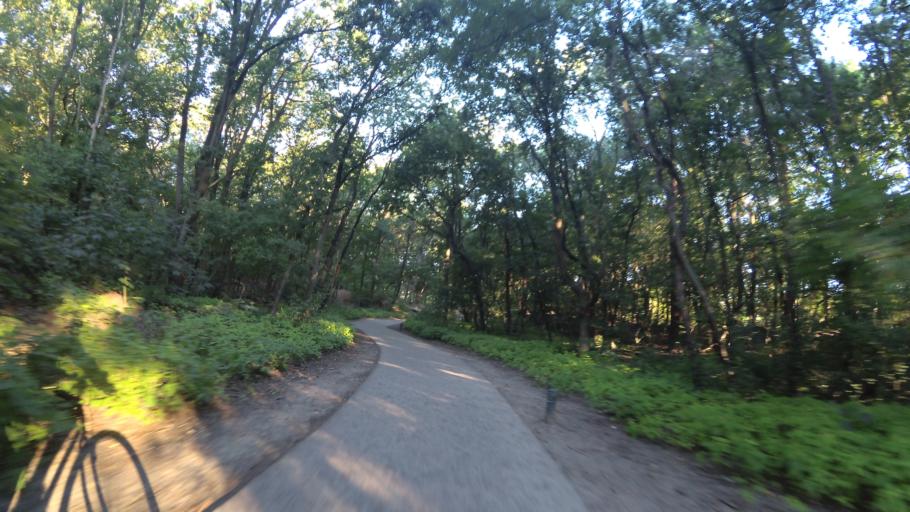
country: NL
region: North Brabant
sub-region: Gemeente Loon op Zand
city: Loon op Zand
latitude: 51.6479
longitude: 5.0422
